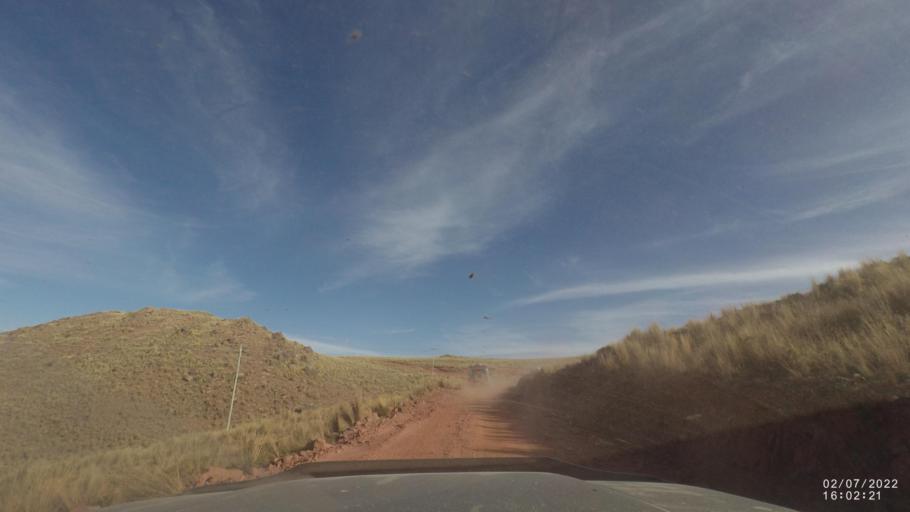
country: BO
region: Cochabamba
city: Irpa Irpa
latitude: -17.9093
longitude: -66.4406
